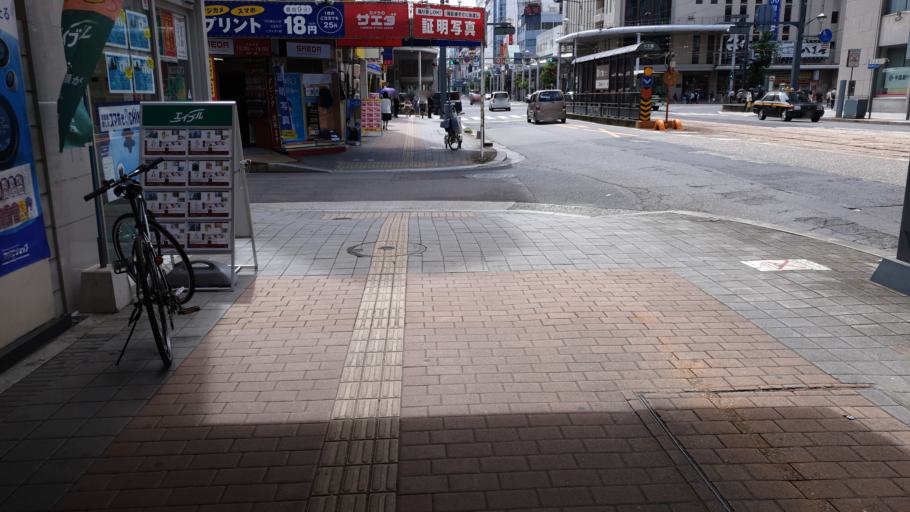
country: JP
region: Hiroshima
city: Hiroshima-shi
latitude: 34.3945
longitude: 132.4638
